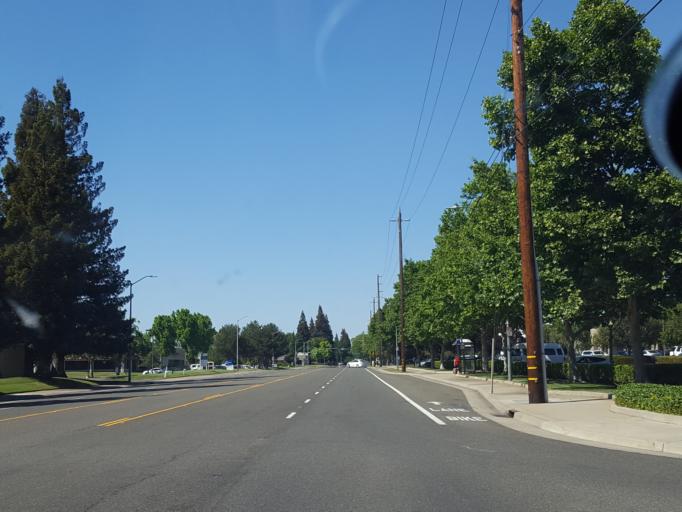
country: US
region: California
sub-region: Sacramento County
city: Rancho Cordova
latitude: 38.5706
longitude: -121.3067
